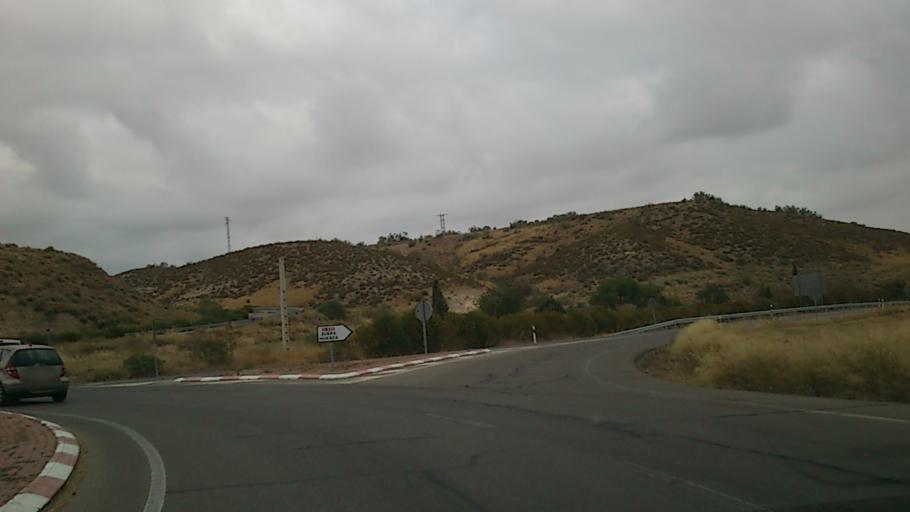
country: ES
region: Aragon
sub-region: Provincia de Zaragoza
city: San Mateo de Gallego
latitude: 41.8296
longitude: -0.7998
